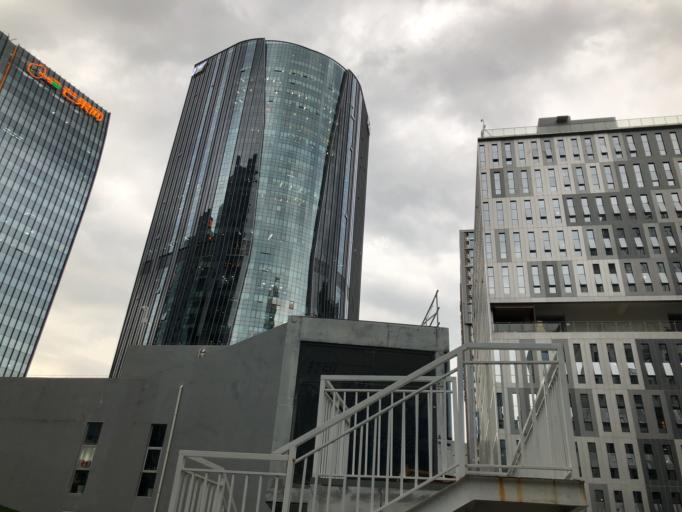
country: CN
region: Guangdong
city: Haikuotiankong
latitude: 22.5262
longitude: 113.9318
